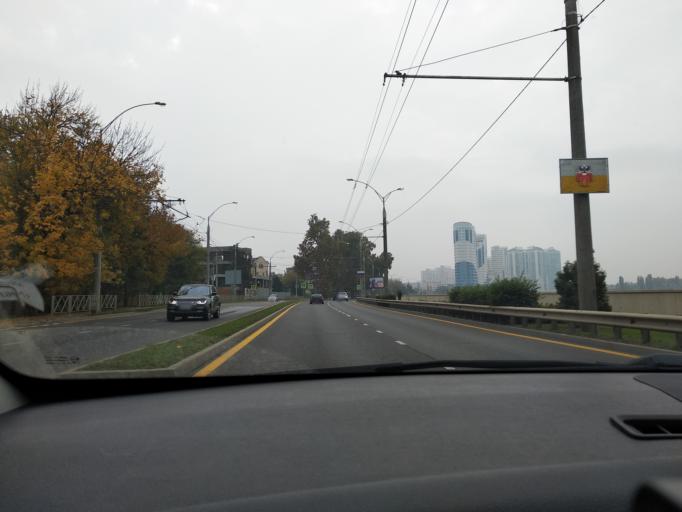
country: RU
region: Krasnodarskiy
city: Krasnodar
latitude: 45.0327
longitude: 38.9584
